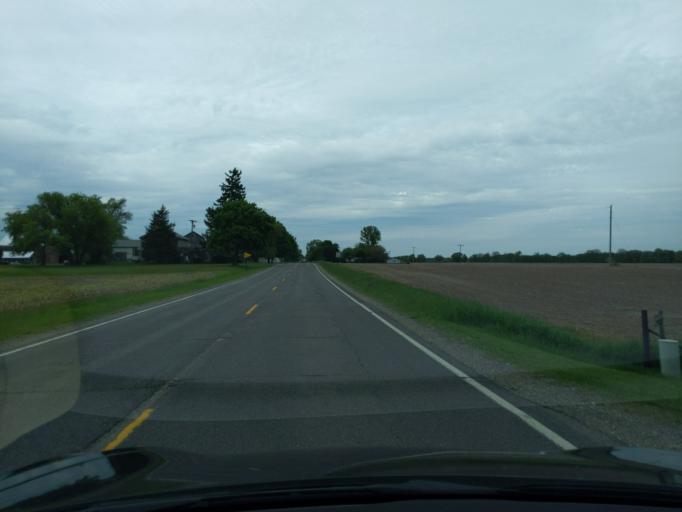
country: US
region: Michigan
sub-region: Ingham County
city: Leslie
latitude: 42.4826
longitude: -84.3562
